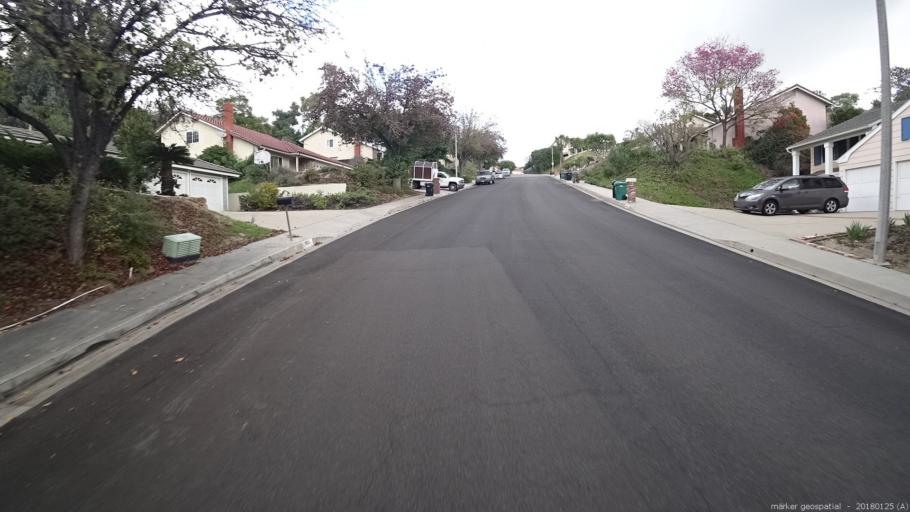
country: US
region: California
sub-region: Los Angeles County
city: Diamond Bar
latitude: 33.9933
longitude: -117.8284
